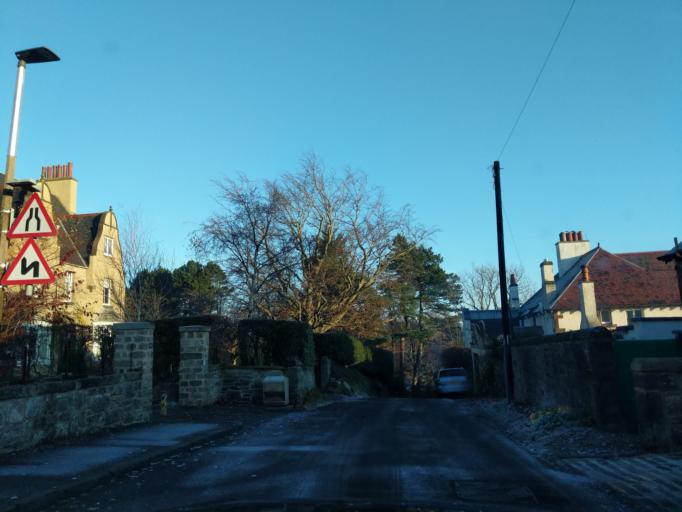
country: GB
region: Scotland
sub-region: Edinburgh
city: Colinton
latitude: 55.9091
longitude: -3.2594
